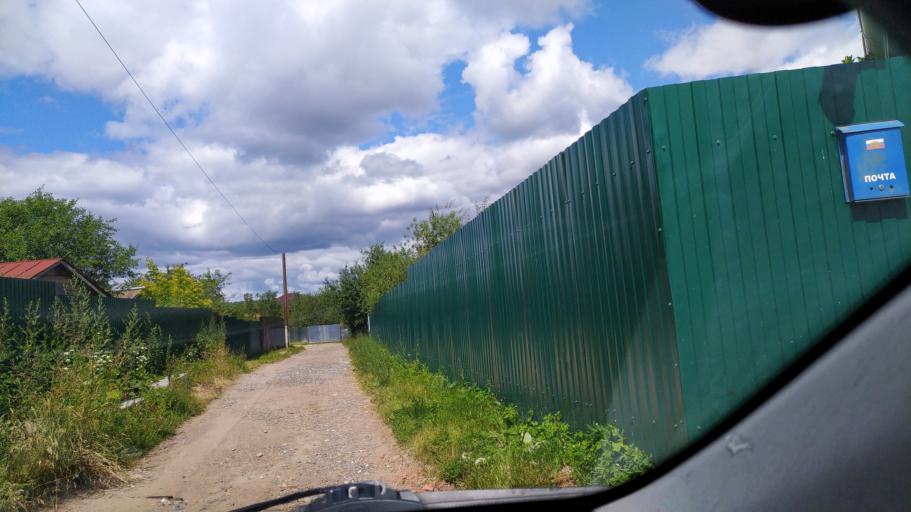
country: RU
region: Chuvashia
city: Novyye Lapsary
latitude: 56.1128
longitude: 47.1750
